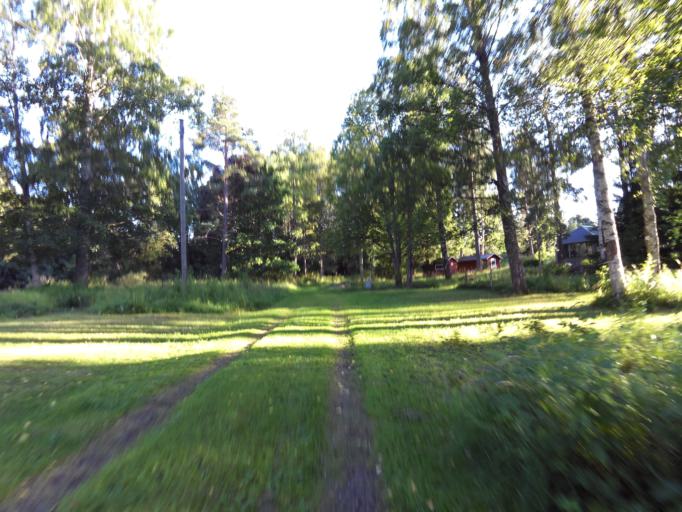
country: SE
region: Gaevleborg
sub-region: Gavle Kommun
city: Gavle
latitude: 60.7090
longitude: 17.1529
